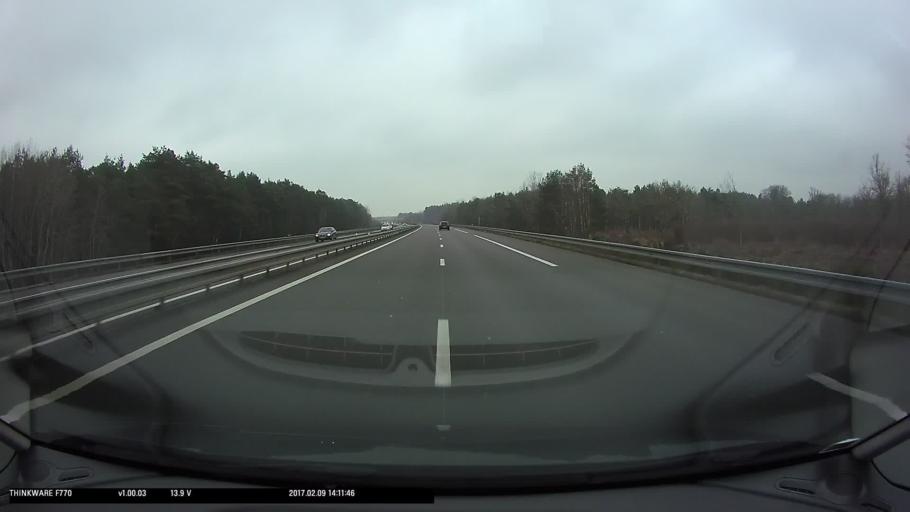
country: FR
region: Centre
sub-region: Departement du Loir-et-Cher
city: Salbris
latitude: 47.4055
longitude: 2.0290
